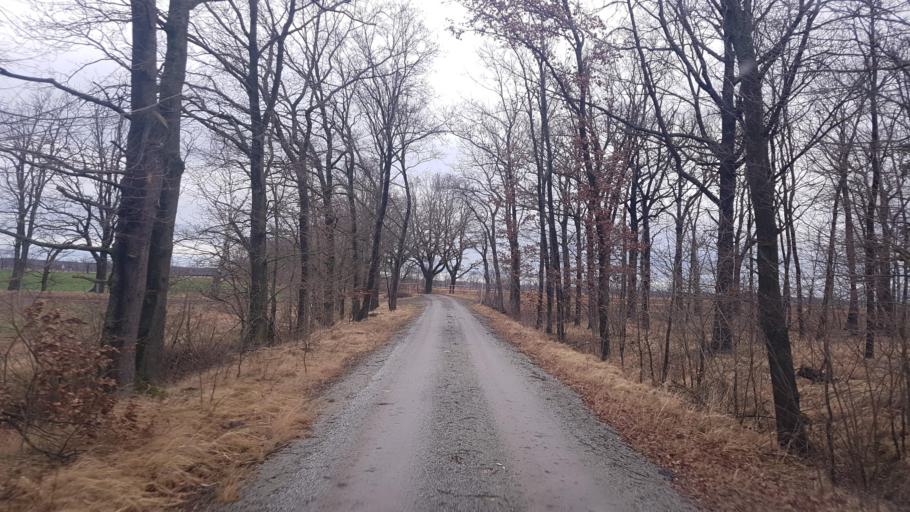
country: DE
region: Brandenburg
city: Plessa
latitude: 51.4472
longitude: 13.6519
